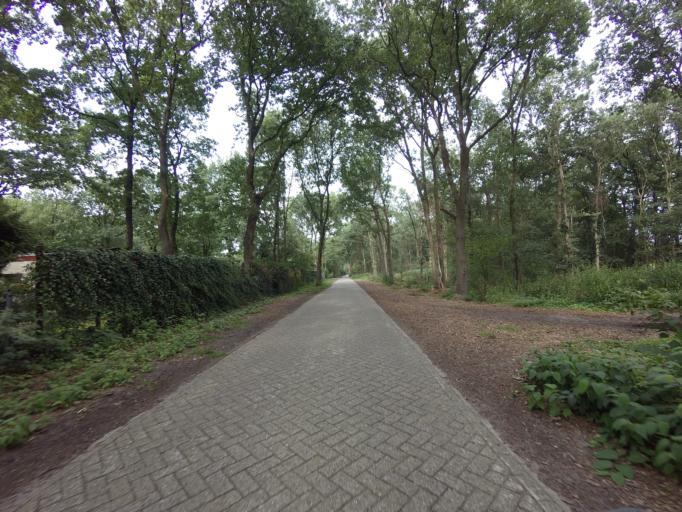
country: NL
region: Friesland
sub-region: Gemeente Weststellingwerf
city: Noordwolde
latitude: 52.9236
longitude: 6.2557
